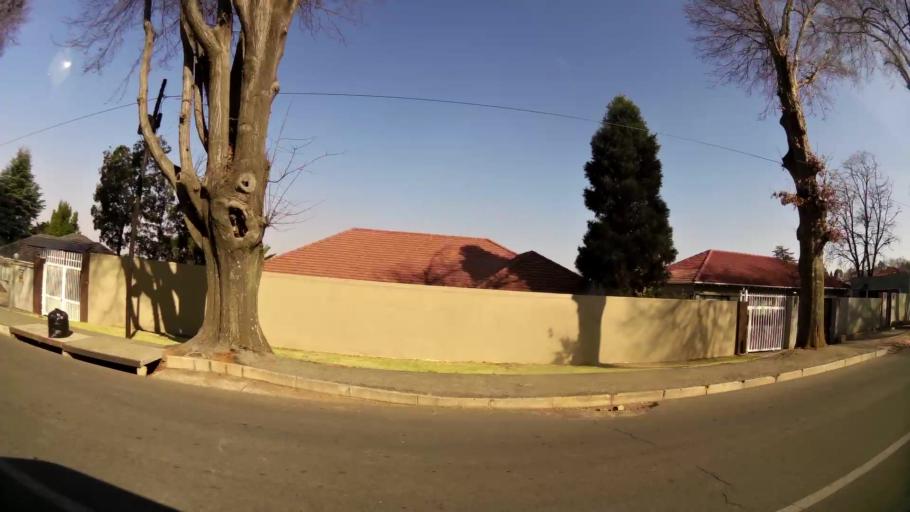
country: ZA
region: Gauteng
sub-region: City of Johannesburg Metropolitan Municipality
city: Johannesburg
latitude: -26.1707
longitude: 28.1001
